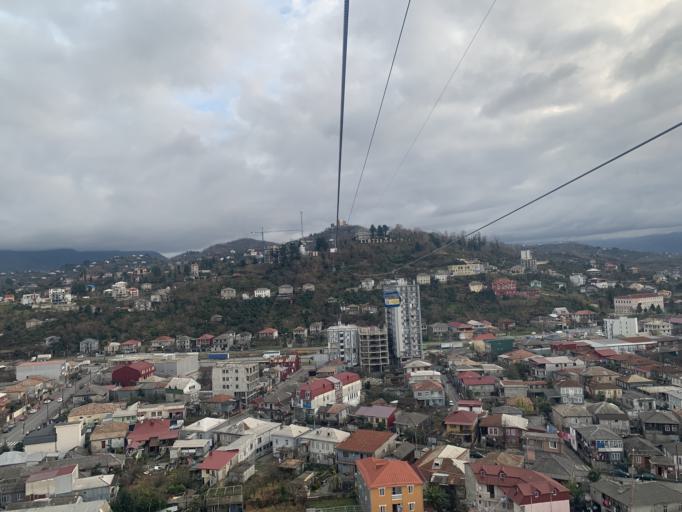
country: GE
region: Ajaria
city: Batumi
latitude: 41.6421
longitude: 41.6482
